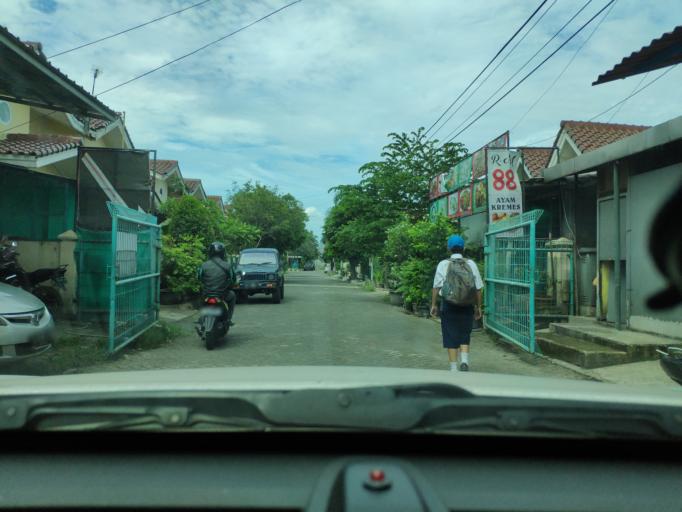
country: ID
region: West Java
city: Ciputat
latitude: -6.2200
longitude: 106.7090
